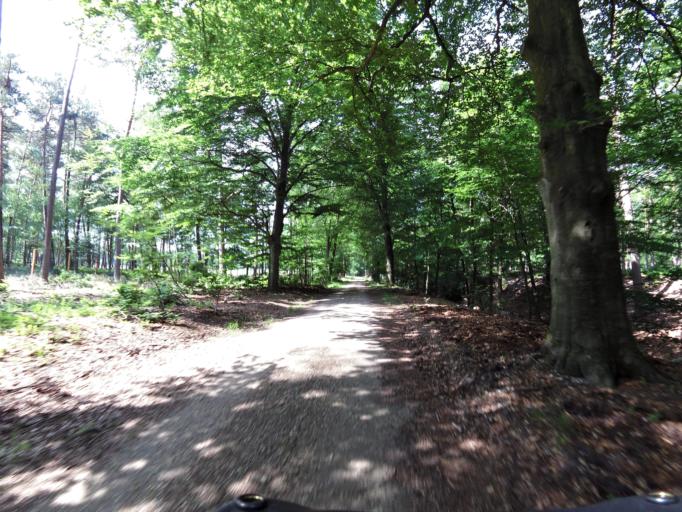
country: NL
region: Gelderland
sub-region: Gemeente Apeldoorn
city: Loenen
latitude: 52.1152
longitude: 5.9883
